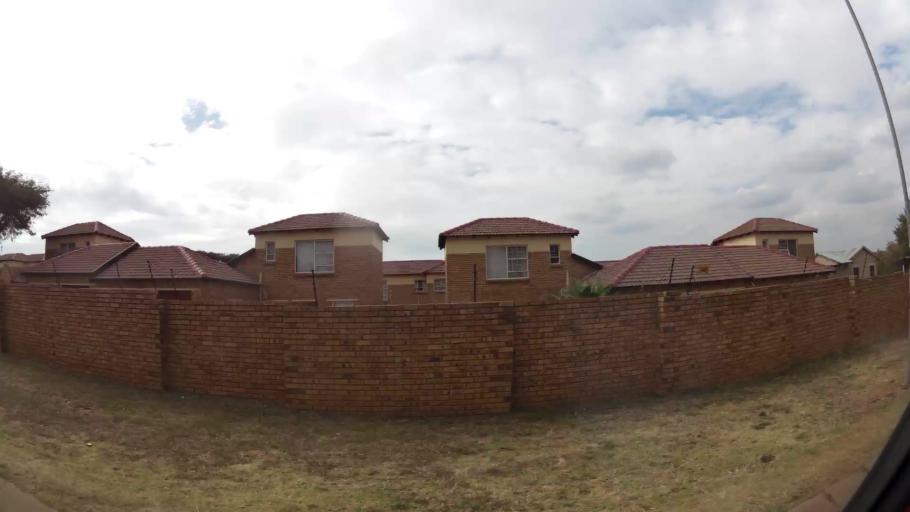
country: ZA
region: Gauteng
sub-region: City of Johannesburg Metropolitan Municipality
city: Roodepoort
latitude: -26.0966
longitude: 27.8786
